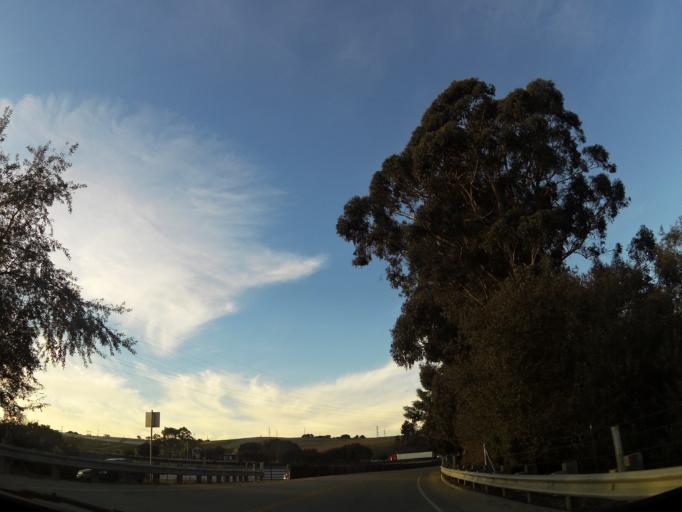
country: US
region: California
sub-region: Monterey County
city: Prunedale
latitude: 36.7713
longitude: -121.6022
